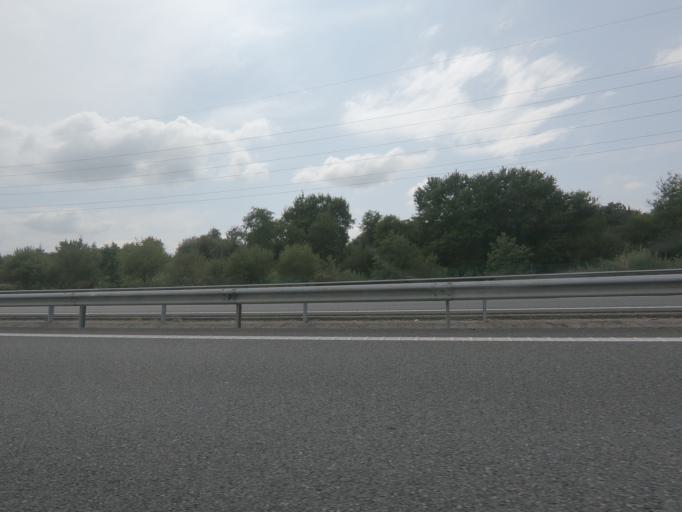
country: ES
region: Galicia
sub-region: Provincia de Pontevedra
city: Porrino
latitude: 42.1416
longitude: -8.6247
